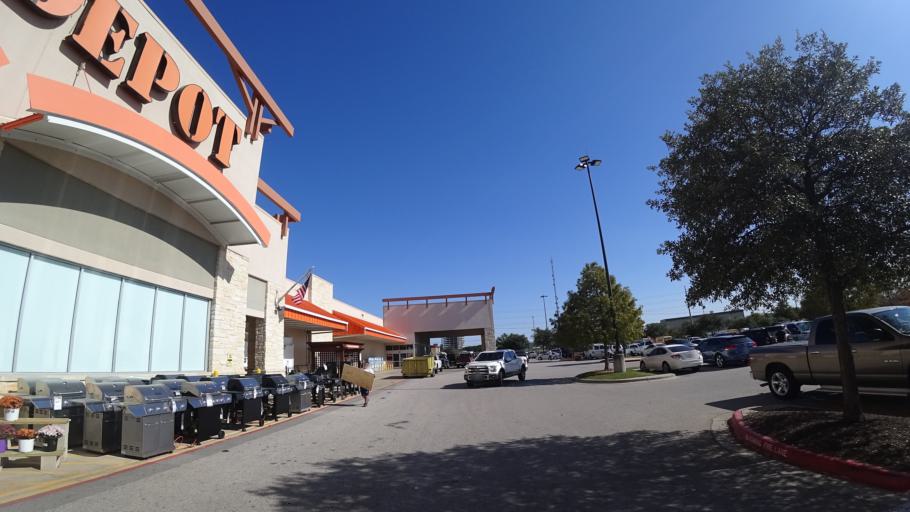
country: US
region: Texas
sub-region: Williamson County
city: Jollyville
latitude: 30.3934
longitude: -97.7317
